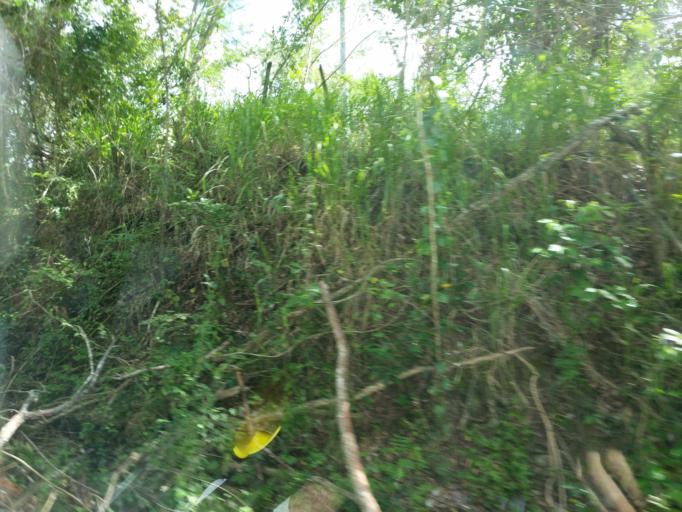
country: PR
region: Coamo
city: Coamo
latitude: 18.0987
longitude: -66.3979
